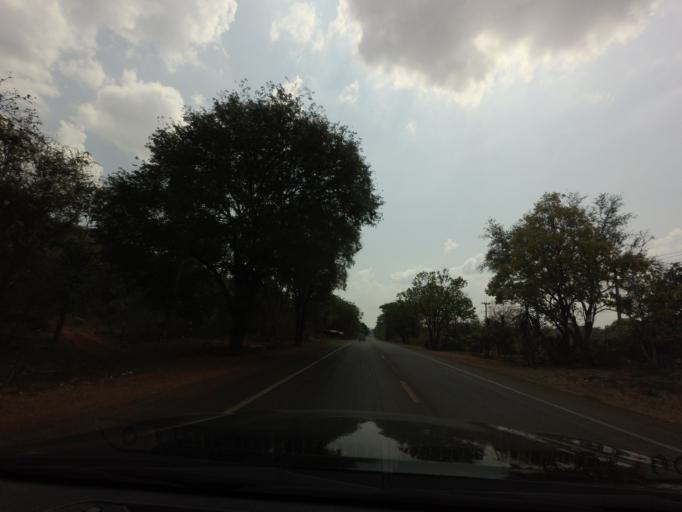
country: TH
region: Kanchanaburi
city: Sai Yok
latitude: 14.1492
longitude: 99.1437
